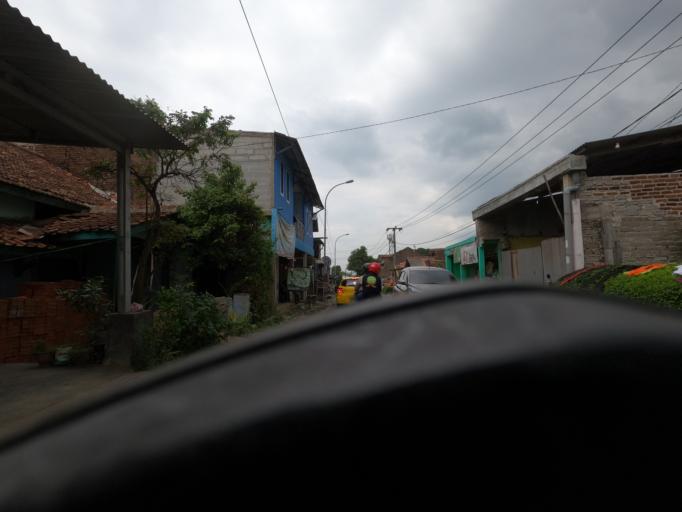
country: ID
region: West Java
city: Padalarang
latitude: -6.8417
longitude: 107.5020
